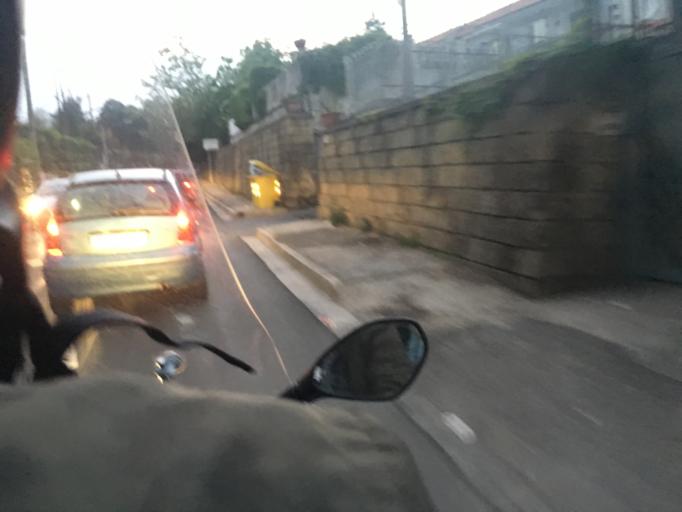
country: IT
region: Campania
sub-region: Provincia di Napoli
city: Torre Caracciolo
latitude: 40.8633
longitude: 14.2092
